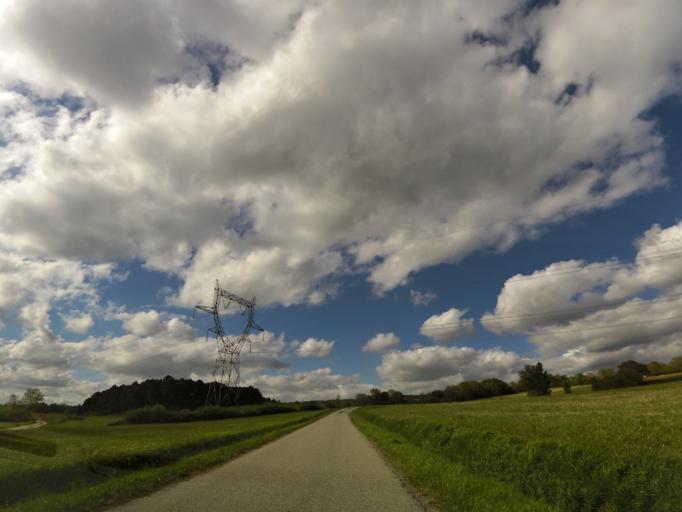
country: FR
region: Languedoc-Roussillon
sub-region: Departement de l'Aude
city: Saint-Martin-Lalande
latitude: 43.3602
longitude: 2.0553
